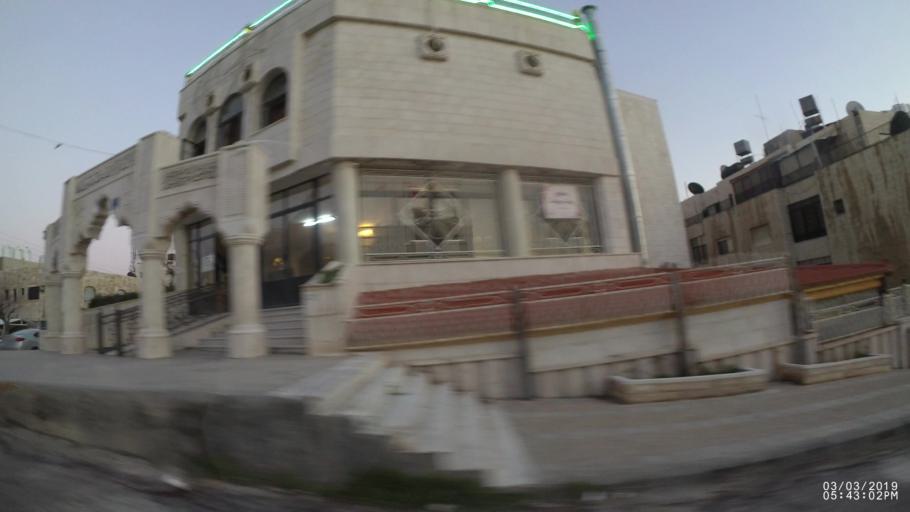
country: JO
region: Amman
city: Al Jubayhah
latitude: 31.9851
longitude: 35.8911
